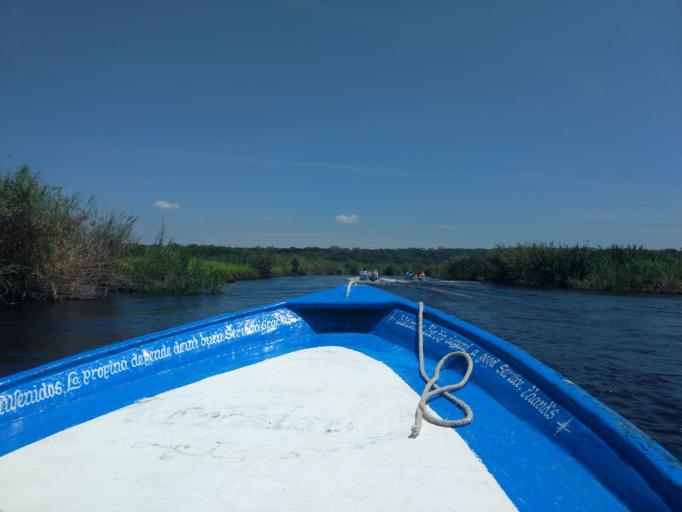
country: MX
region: Nayarit
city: San Blas
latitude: 21.5360
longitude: -105.2336
